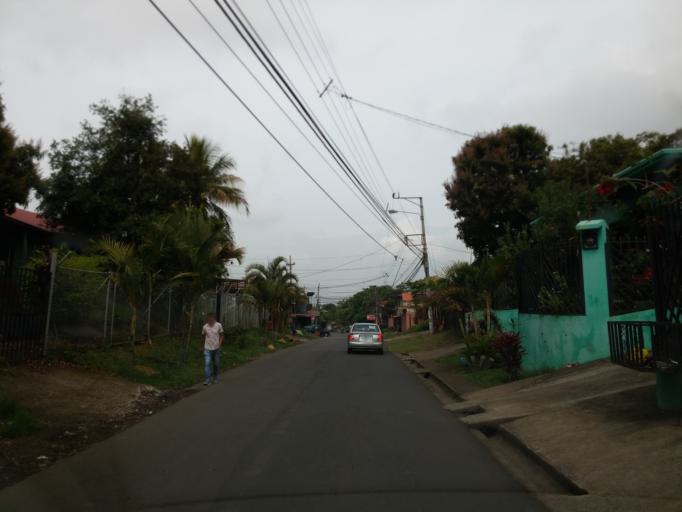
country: CR
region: Heredia
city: Llorente
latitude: 10.0157
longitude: -84.1682
